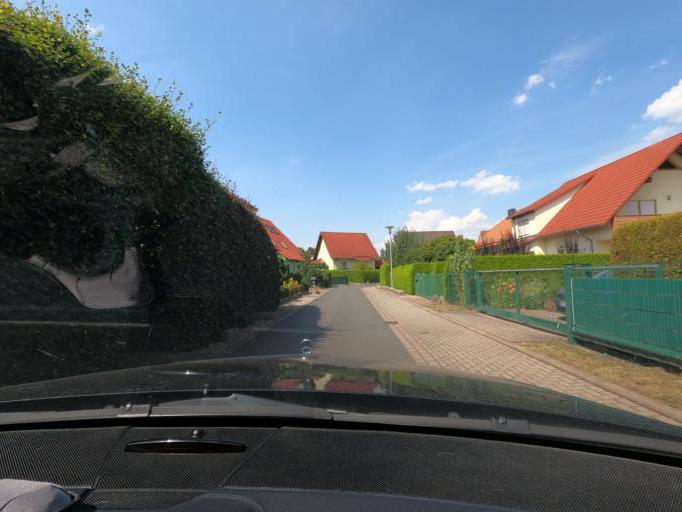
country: DE
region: Thuringia
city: Nordhausen
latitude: 51.5141
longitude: 10.7640
